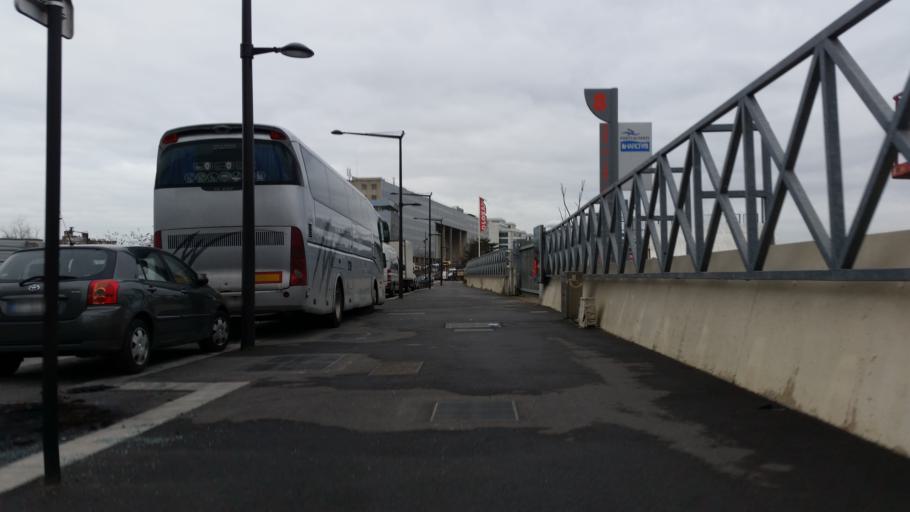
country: FR
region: Ile-de-France
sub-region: Departement du Val-de-Marne
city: Charenton-le-Pont
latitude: 48.8176
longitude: 2.4042
